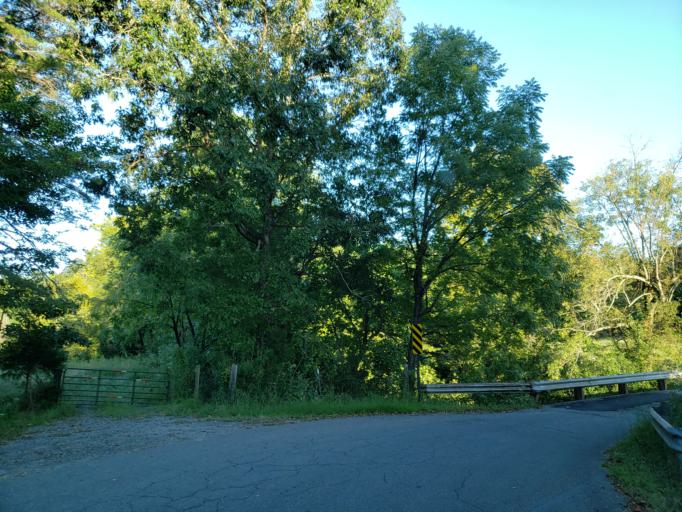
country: US
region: Georgia
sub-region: Bartow County
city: Rydal
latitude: 34.4036
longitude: -84.6720
